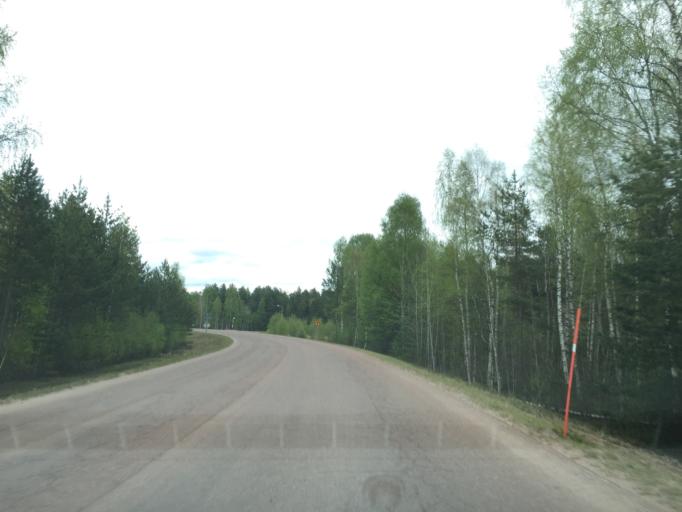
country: SE
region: Dalarna
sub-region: Mora Kommun
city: Mora
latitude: 61.0241
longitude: 14.5039
